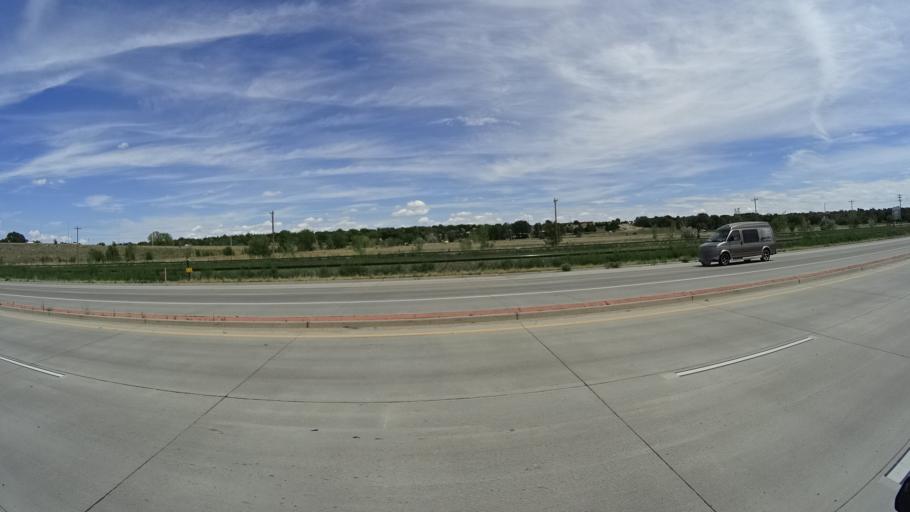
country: US
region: Colorado
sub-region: El Paso County
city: Security-Widefield
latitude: 38.7206
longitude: -104.7176
